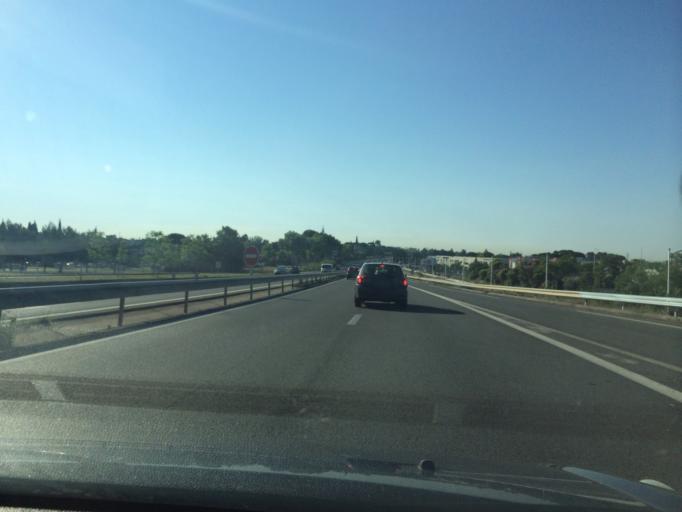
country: FR
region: Languedoc-Roussillon
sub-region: Departement de l'Herault
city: Juvignac
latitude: 43.6184
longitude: 3.7932
